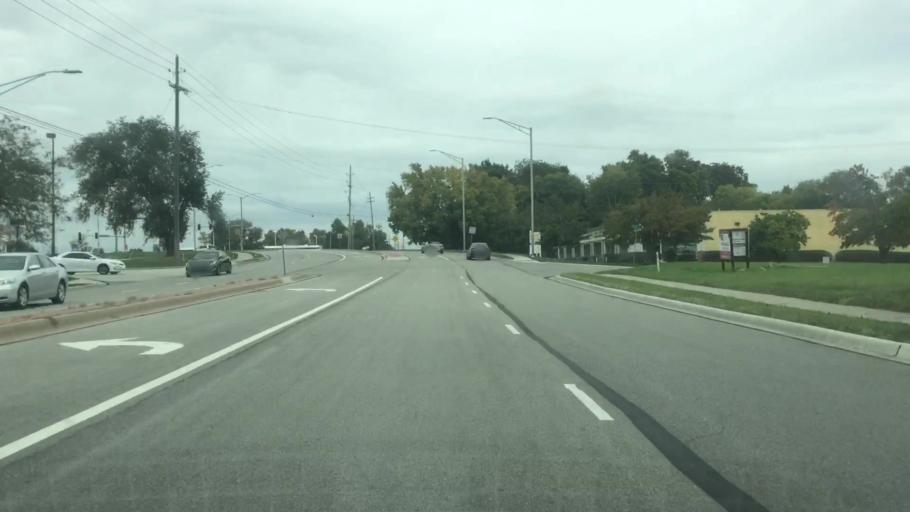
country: US
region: Kansas
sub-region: Johnson County
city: Lenexa
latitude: 38.9149
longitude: -94.7609
